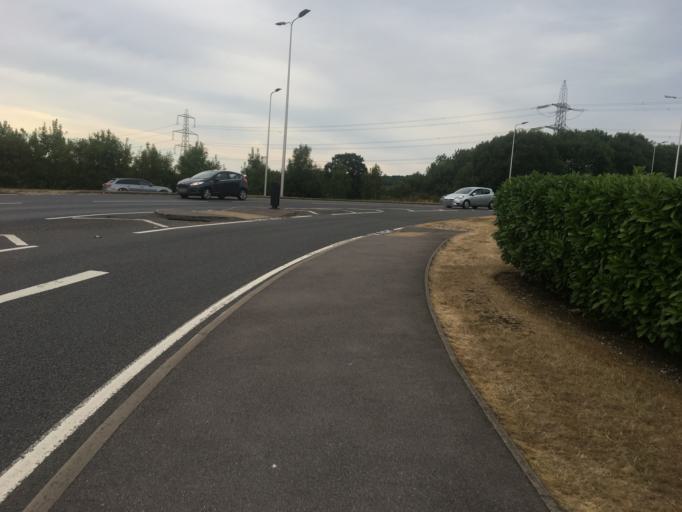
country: GB
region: England
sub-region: West Berkshire
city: Theale
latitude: 51.4368
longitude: -1.0704
